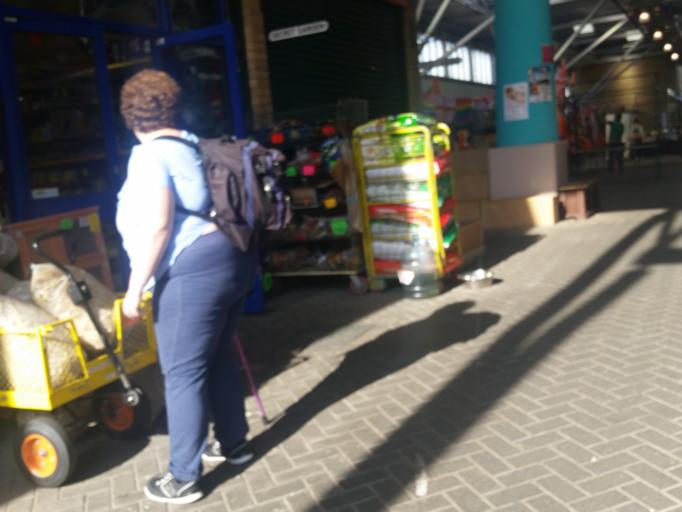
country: GB
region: England
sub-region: Brighton and Hove
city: Brighton
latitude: 50.8314
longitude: -0.1357
